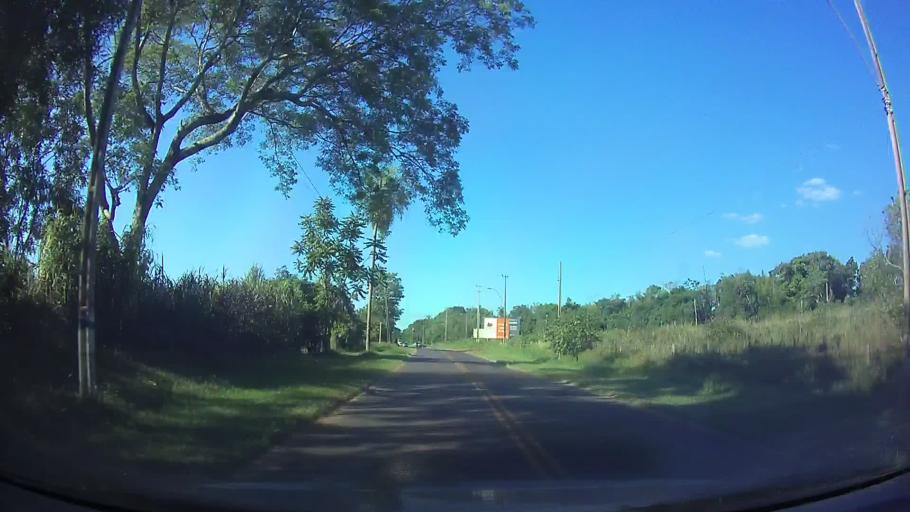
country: PY
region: Cordillera
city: Atyra
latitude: -25.3001
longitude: -57.1852
